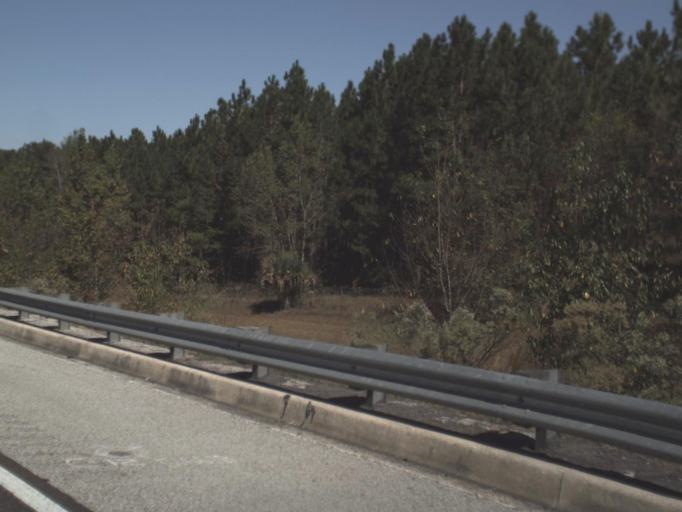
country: US
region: Florida
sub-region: Lake County
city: Minneola
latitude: 28.6058
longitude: -81.7243
